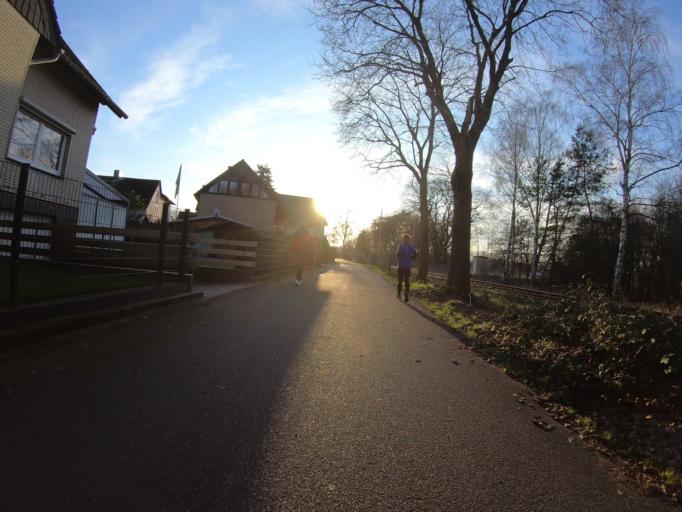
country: DE
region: Lower Saxony
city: Gifhorn
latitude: 52.4862
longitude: 10.5589
